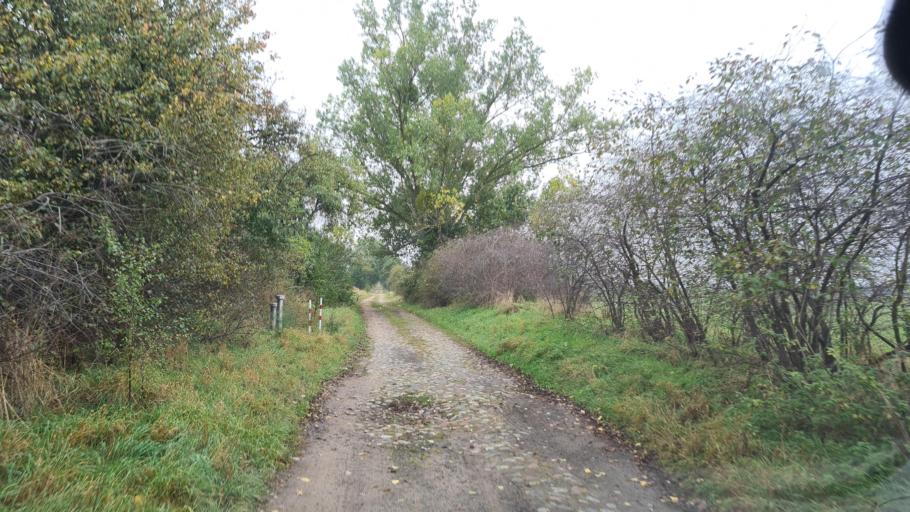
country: DE
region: Brandenburg
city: Furstenwalde
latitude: 52.4279
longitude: 14.0205
